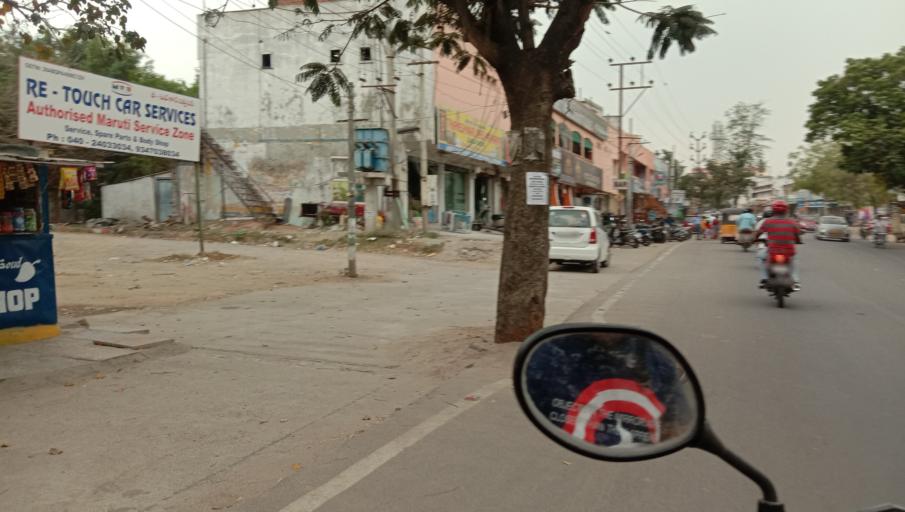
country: IN
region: Telangana
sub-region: Rangareddi
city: Lal Bahadur Nagar
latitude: 17.3759
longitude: 78.5559
